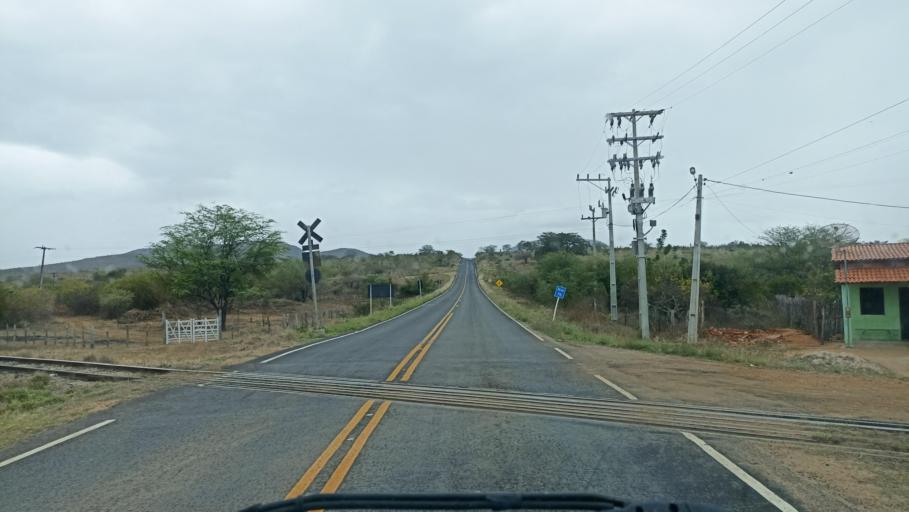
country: BR
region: Bahia
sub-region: Andarai
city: Vera Cruz
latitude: -13.0488
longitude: -40.7485
